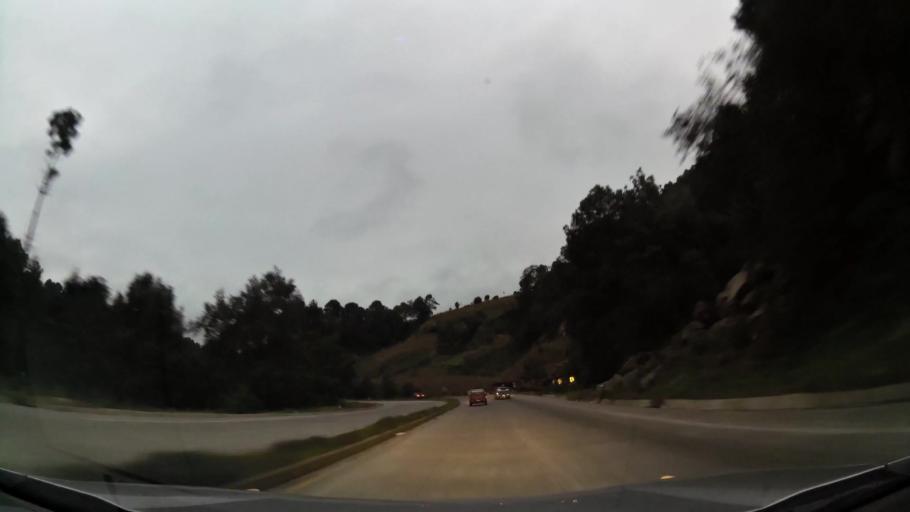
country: GT
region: Chimaltenango
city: Tecpan Guatemala
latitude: 14.8324
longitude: -91.0410
